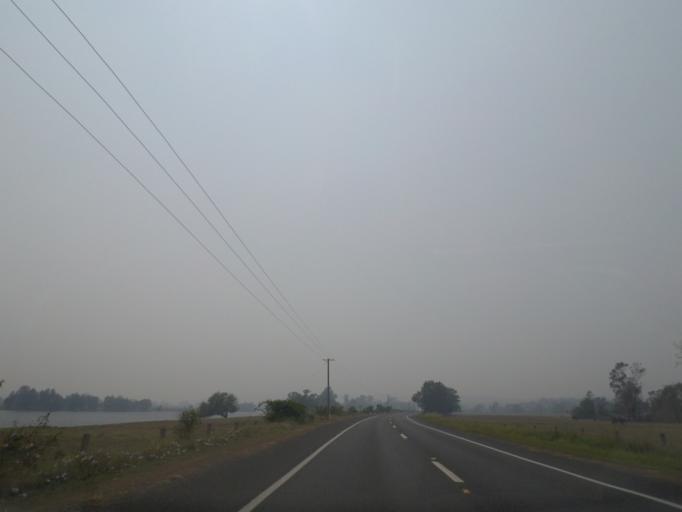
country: AU
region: New South Wales
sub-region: Clarence Valley
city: Maclean
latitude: -29.5654
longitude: 153.1223
